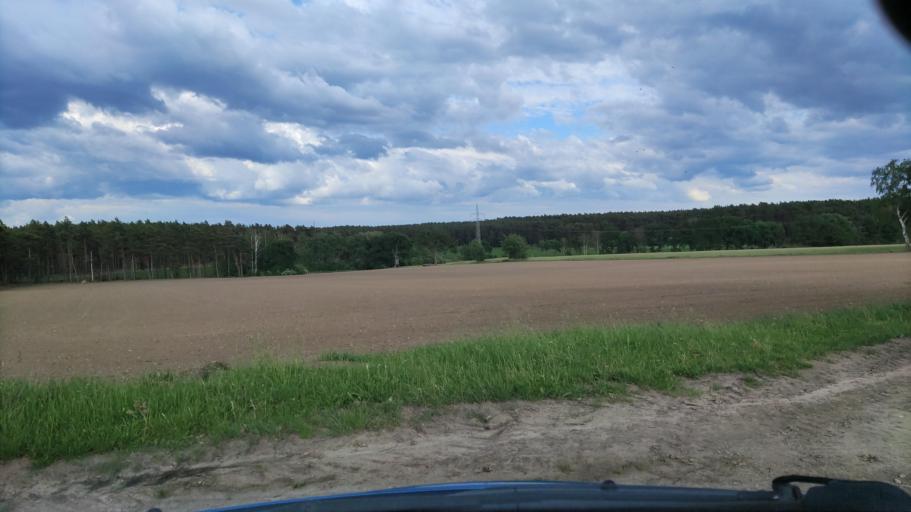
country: DE
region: Lower Saxony
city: Schnega
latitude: 52.9169
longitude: 10.8477
